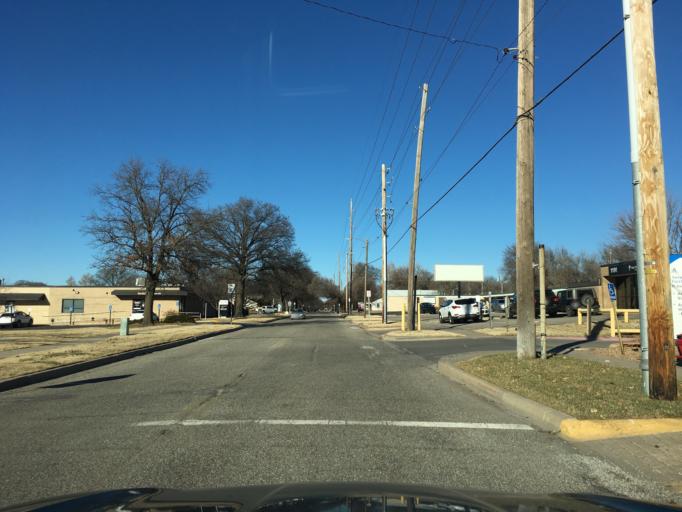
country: US
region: Kansas
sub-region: Sedgwick County
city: Wichita
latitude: 37.6664
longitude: -97.2942
